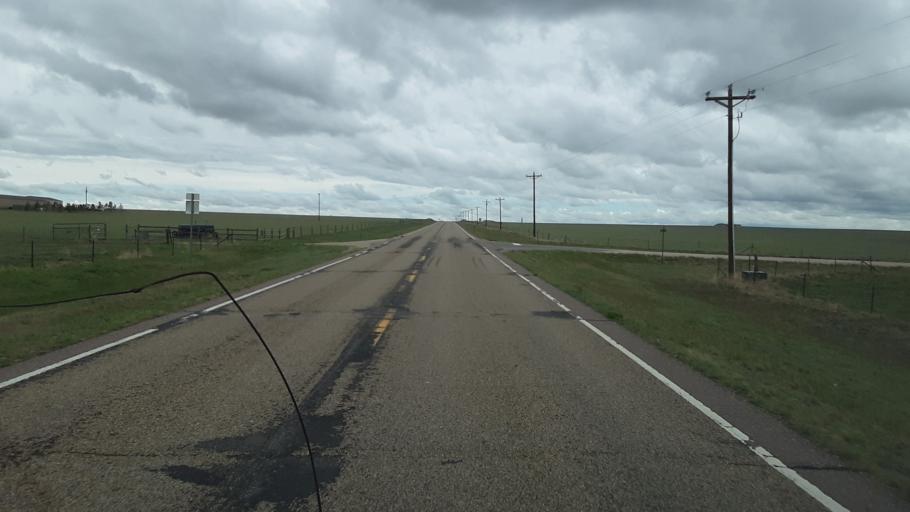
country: US
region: Colorado
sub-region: El Paso County
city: Ellicott
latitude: 38.8399
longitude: -104.0161
